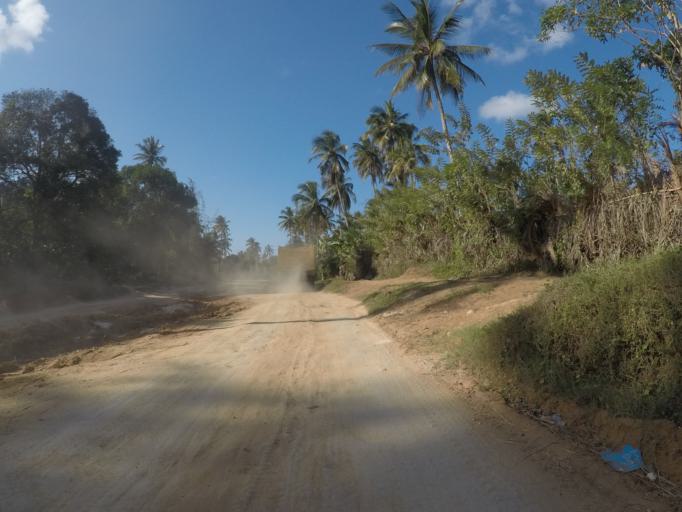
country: TZ
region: Zanzibar Central/South
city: Koani
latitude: -6.1720
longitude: 39.2852
